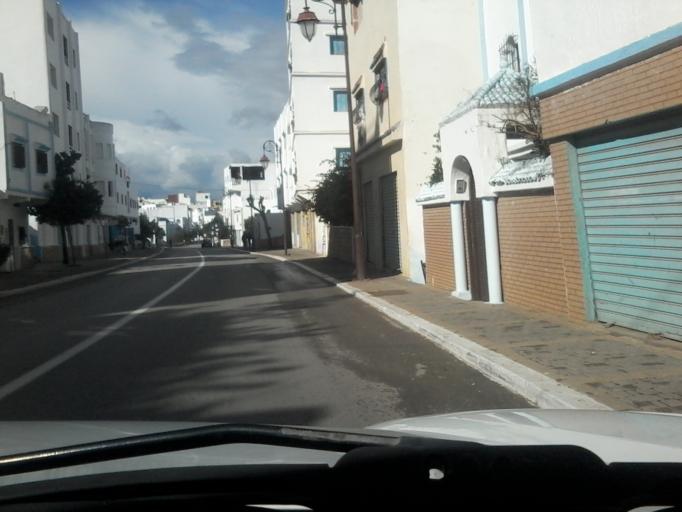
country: MA
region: Tanger-Tetouan
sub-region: Tetouan
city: Martil
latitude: 35.6791
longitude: -5.3250
